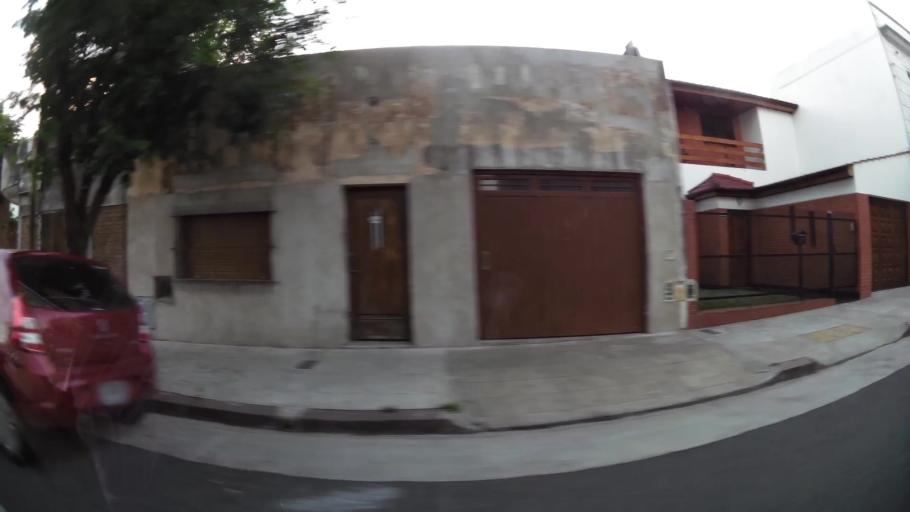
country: AR
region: Buenos Aires F.D.
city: Colegiales
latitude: -34.5484
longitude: -58.4748
